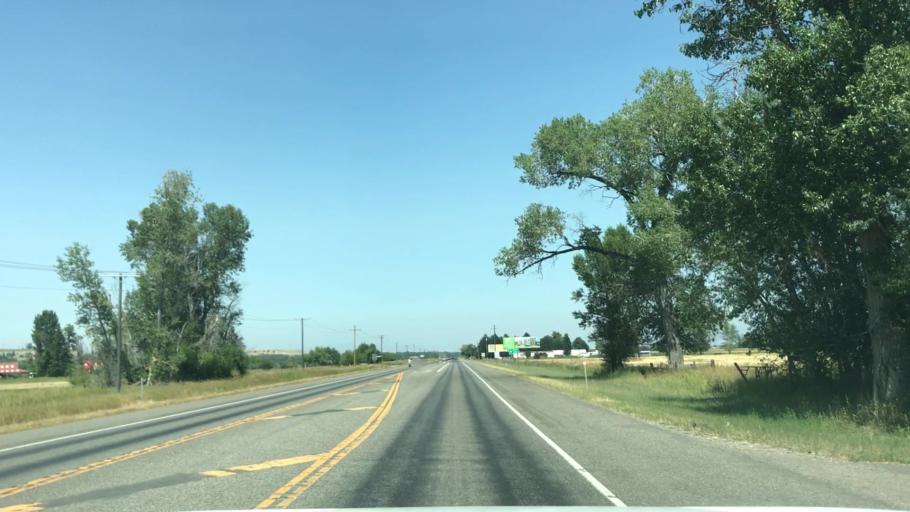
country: US
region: Montana
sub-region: Gallatin County
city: Four Corners
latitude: 45.6215
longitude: -111.1969
